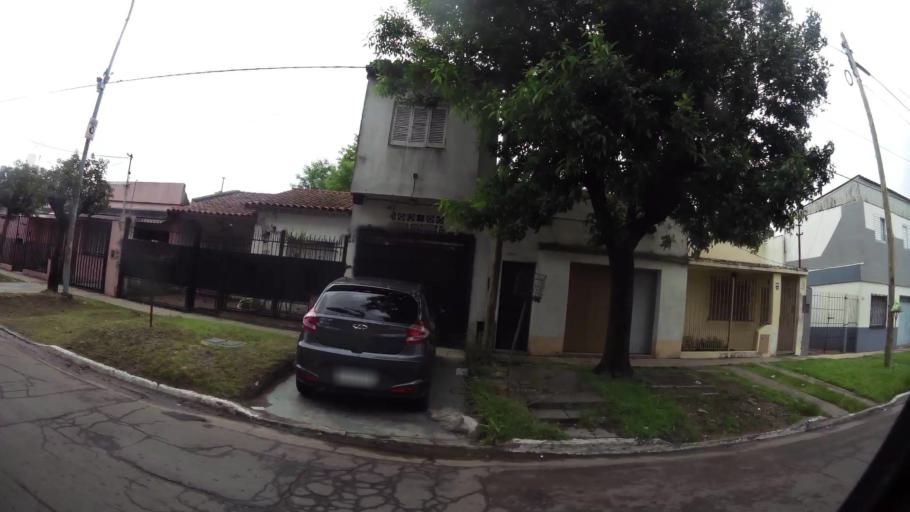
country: AR
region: Buenos Aires
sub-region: Partido de Lanus
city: Lanus
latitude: -34.7288
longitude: -58.3775
